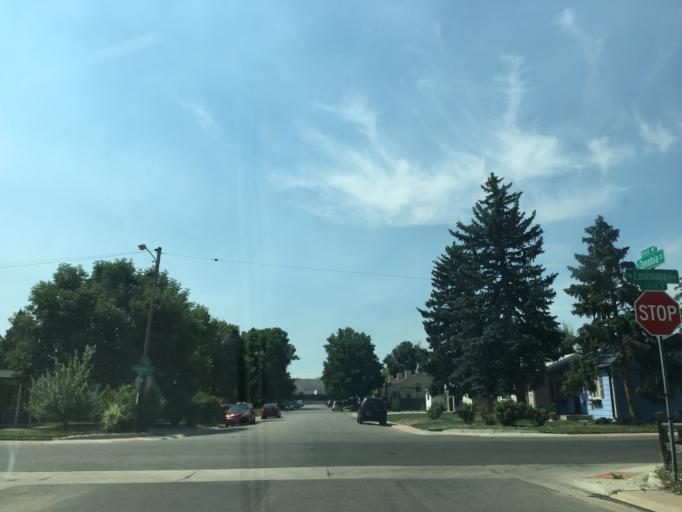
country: US
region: Colorado
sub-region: Jefferson County
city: Lakewood
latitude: 39.6935
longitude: -105.0519
